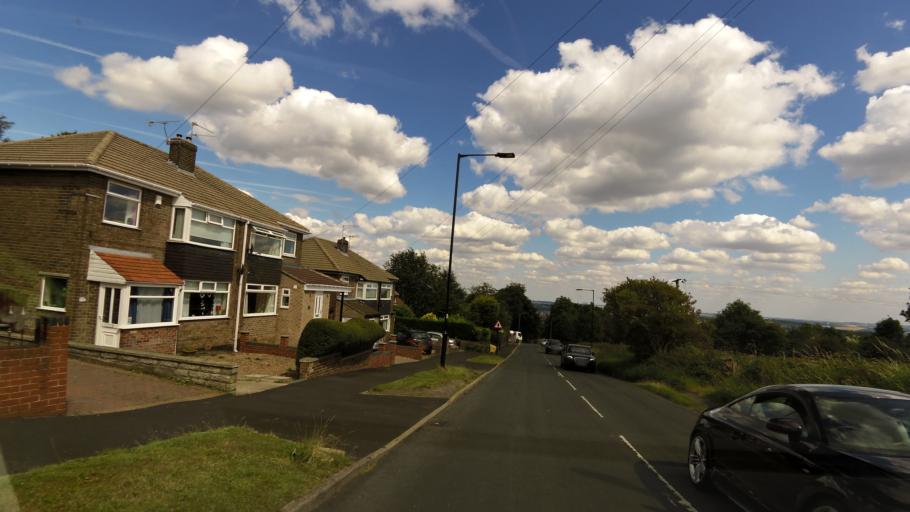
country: GB
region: England
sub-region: Sheffield
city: Oughtibridge
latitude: 53.4368
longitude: -1.5010
